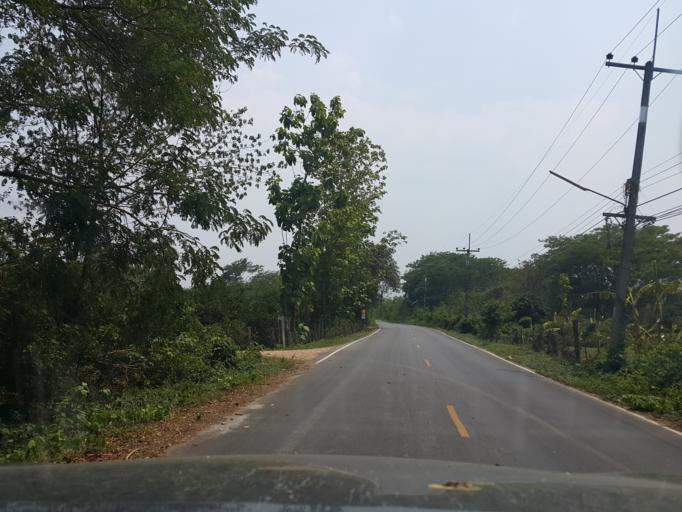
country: TH
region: Lampang
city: Mae Phrik
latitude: 17.5108
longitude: 99.1354
